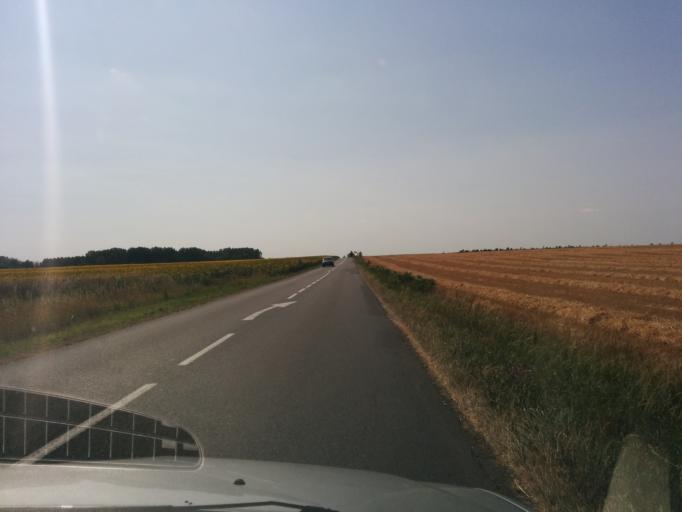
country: FR
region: Poitou-Charentes
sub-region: Departement de la Vienne
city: Saint-Jean-de-Sauves
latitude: 46.8042
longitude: 0.0536
